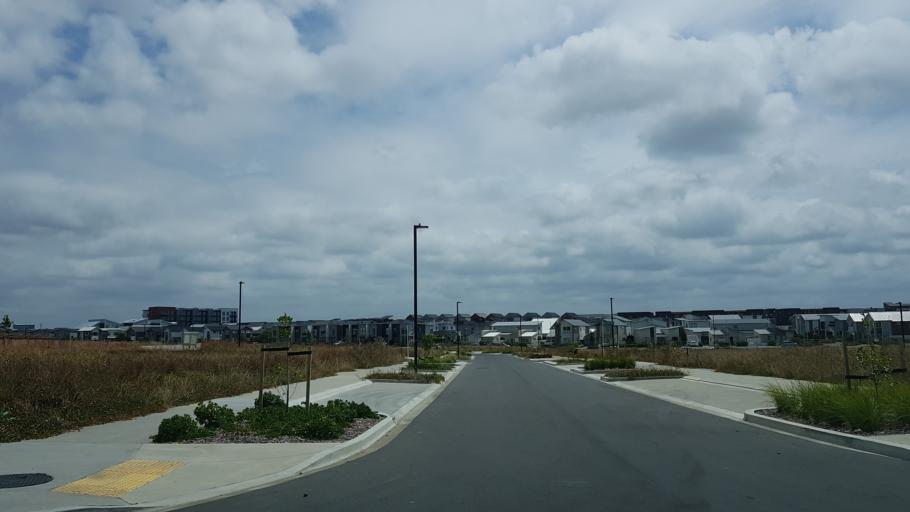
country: NZ
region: Auckland
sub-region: Auckland
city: Rosebank
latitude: -36.7967
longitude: 174.6621
